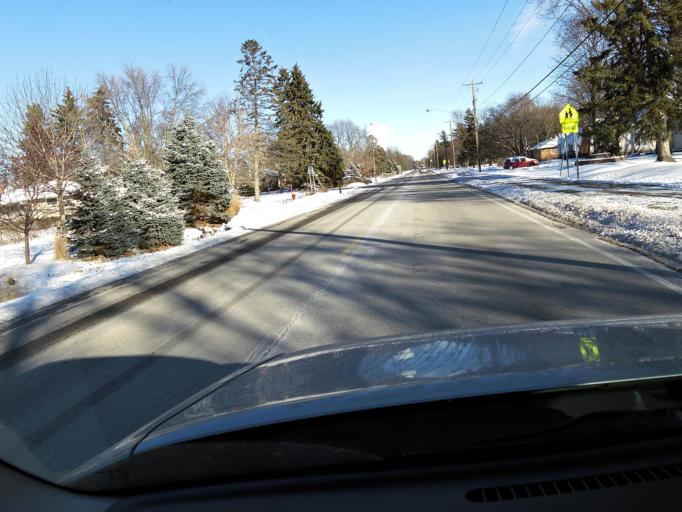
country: US
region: Minnesota
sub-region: Ramsey County
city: Maplewood
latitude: 44.9710
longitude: -92.9968
